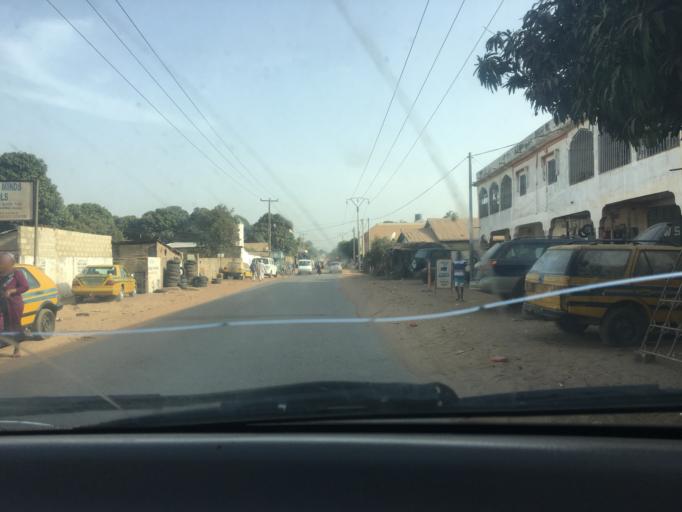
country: GM
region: Western
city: Abuko
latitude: 13.4022
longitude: -16.6734
